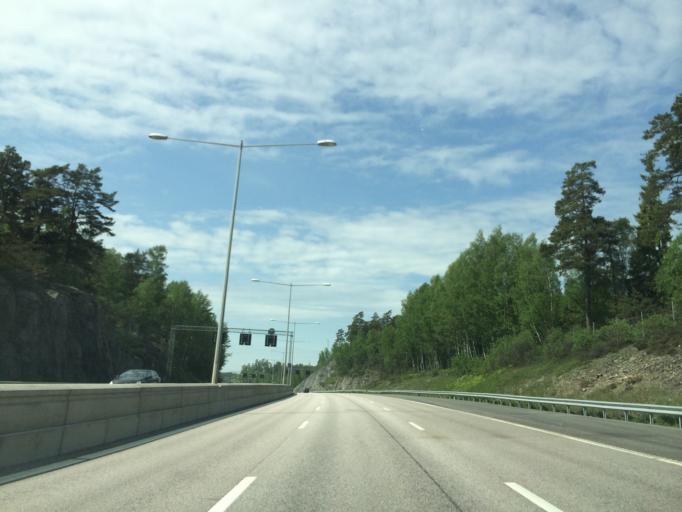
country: SE
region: Stockholm
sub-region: Salems Kommun
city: Ronninge
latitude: 59.2110
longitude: 17.7238
